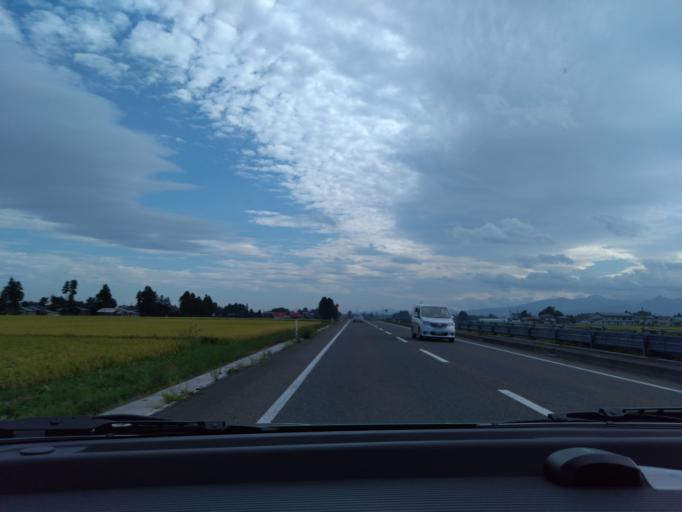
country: JP
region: Iwate
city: Hanamaki
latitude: 39.3612
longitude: 141.0559
